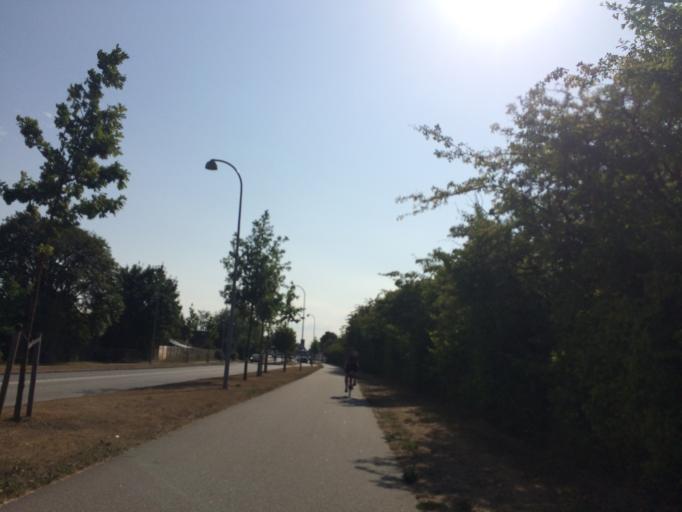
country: DK
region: Capital Region
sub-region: Ishoj Kommune
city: Ishoj
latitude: 55.6109
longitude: 12.3620
